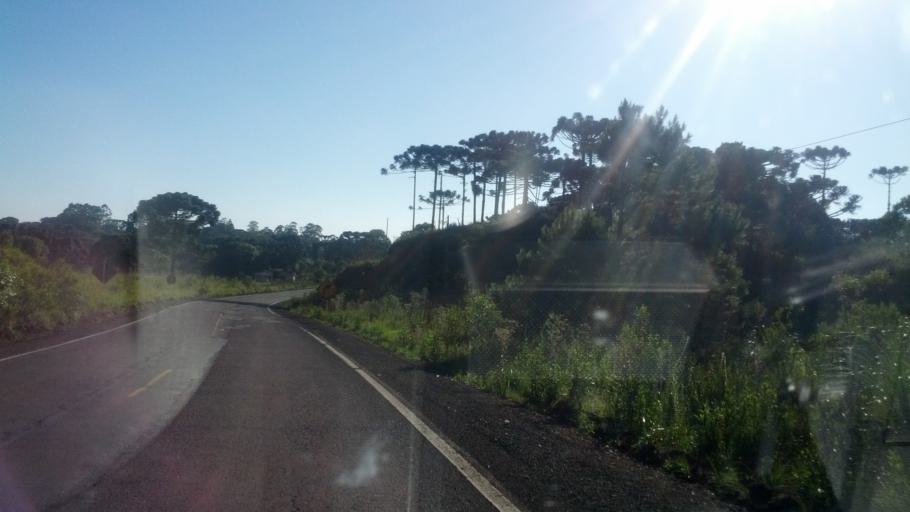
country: BR
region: Santa Catarina
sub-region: Lages
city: Lages
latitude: -27.9138
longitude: -50.5838
